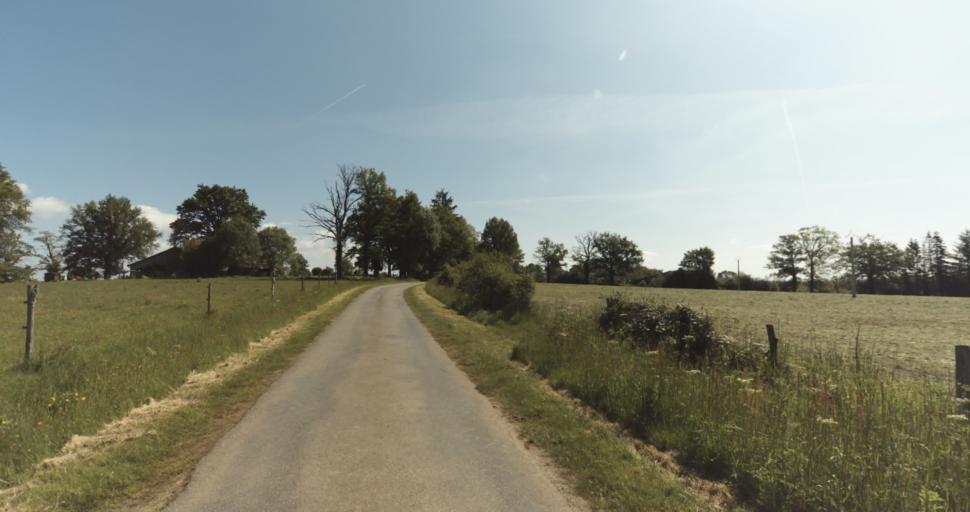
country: FR
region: Limousin
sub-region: Departement de la Haute-Vienne
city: Le Vigen
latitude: 45.7312
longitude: 1.2776
